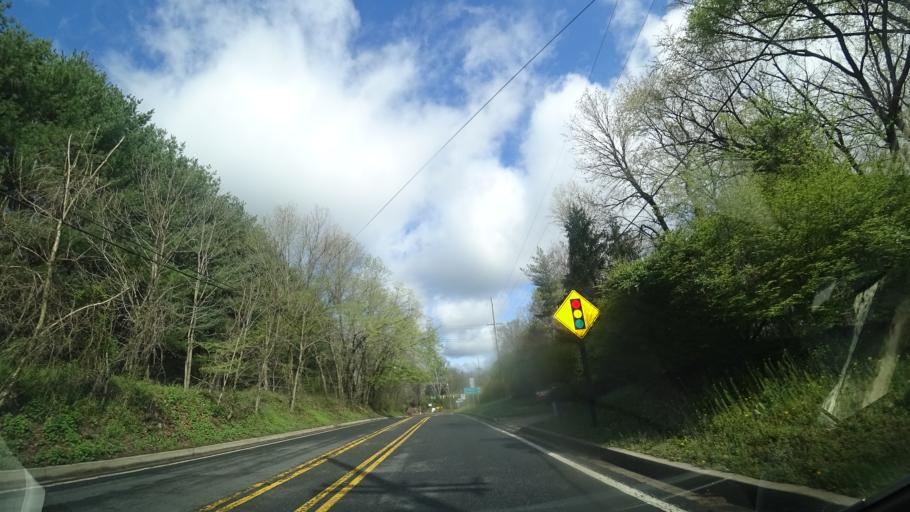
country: US
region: Maryland
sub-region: Montgomery County
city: Poolesville
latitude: 39.2050
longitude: -77.4346
